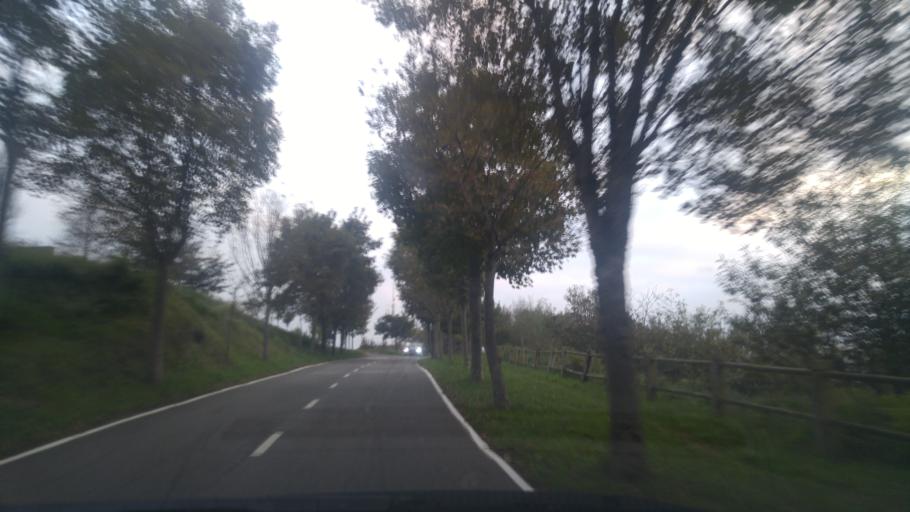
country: ES
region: Asturias
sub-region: Province of Asturias
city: Oviedo
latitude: 43.3862
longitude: -5.8539
